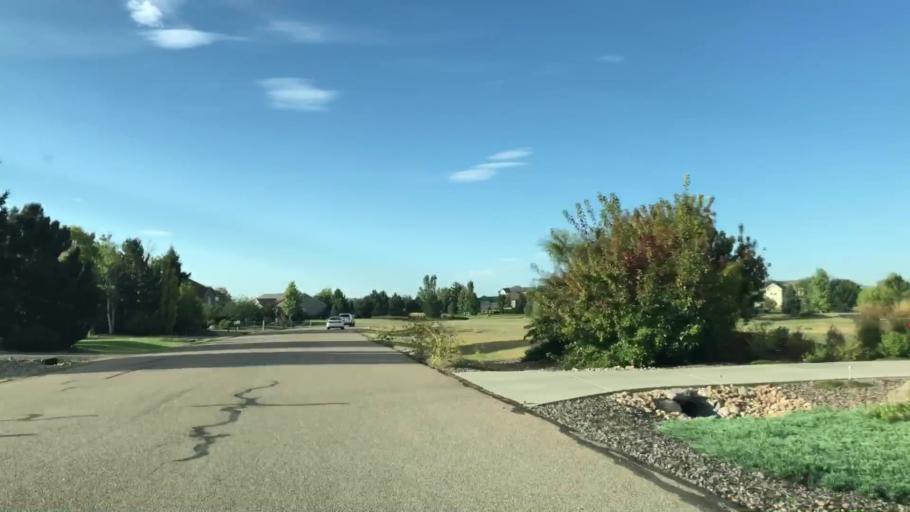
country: US
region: Colorado
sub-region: Weld County
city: Windsor
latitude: 40.4404
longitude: -104.9464
